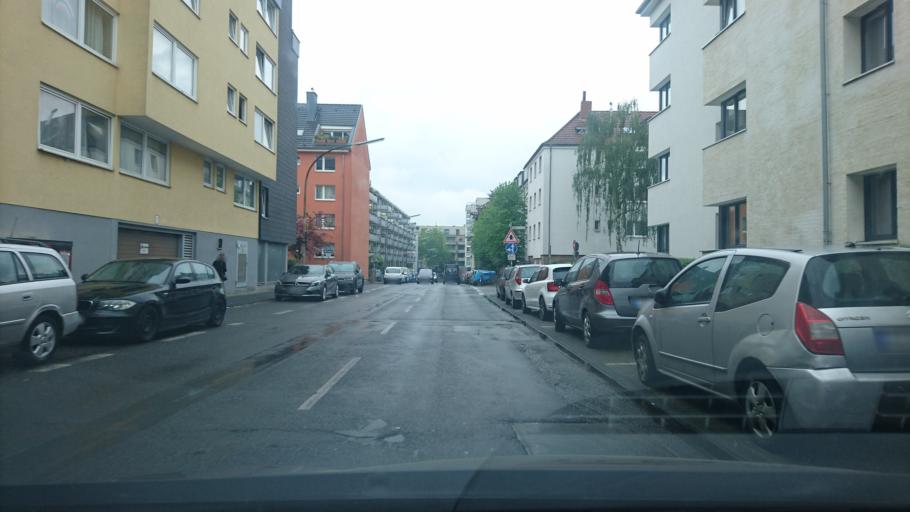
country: DE
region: North Rhine-Westphalia
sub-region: Regierungsbezirk Koln
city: Nippes
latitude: 50.9735
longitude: 6.9483
